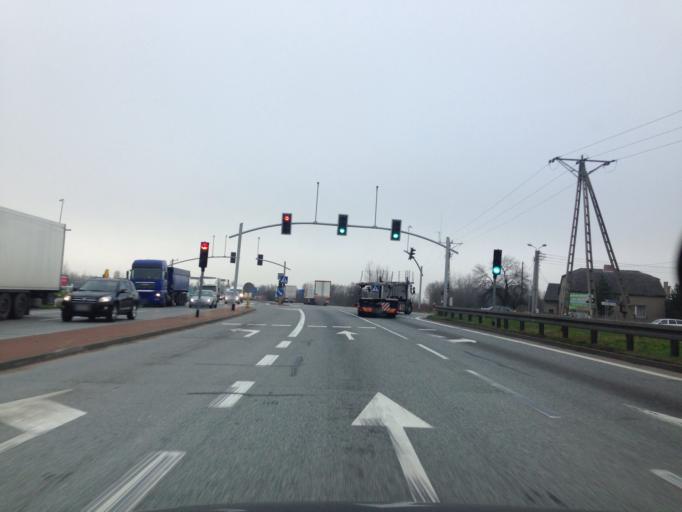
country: PL
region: Silesian Voivodeship
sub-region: Powiat myszkowski
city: Kozieglowy
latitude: 50.5988
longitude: 19.1496
